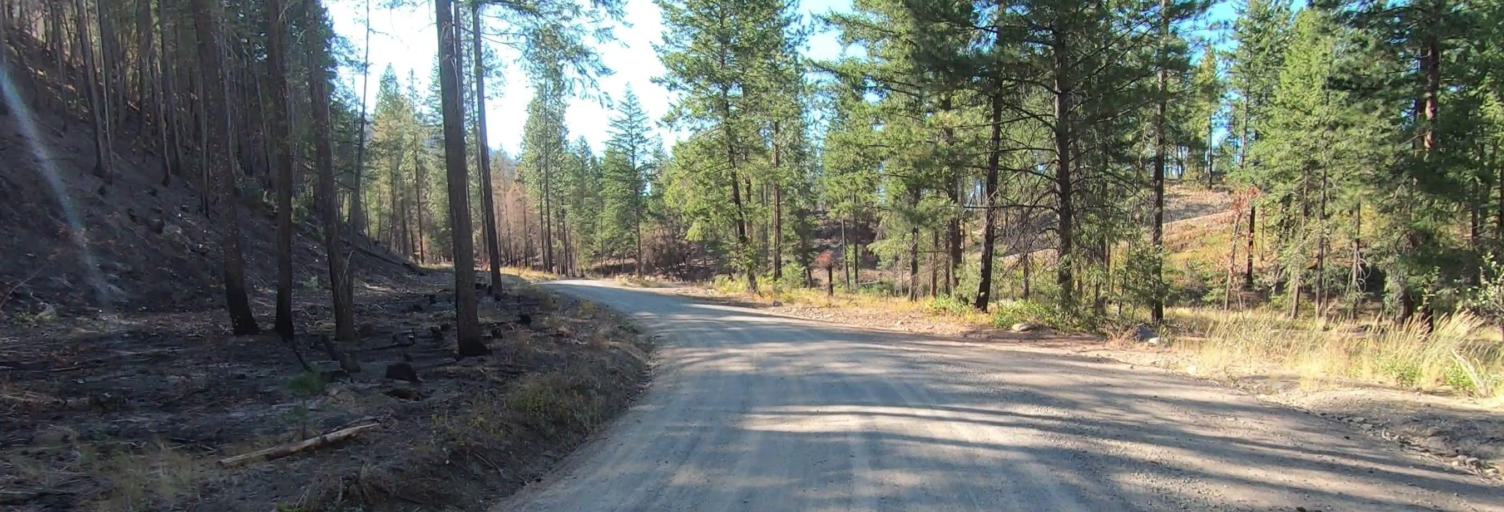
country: US
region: Washington
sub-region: Chelan County
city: Granite Falls
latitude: 48.5054
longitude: -120.2842
